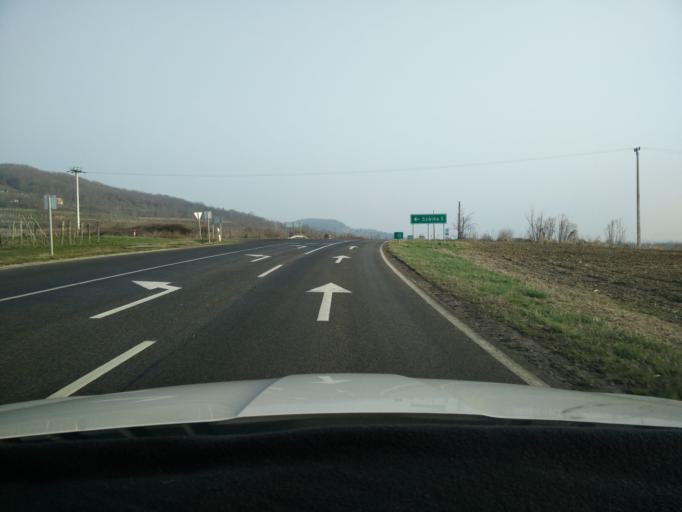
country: HU
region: Tolna
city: Szekszard
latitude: 46.2941
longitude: 18.6859
